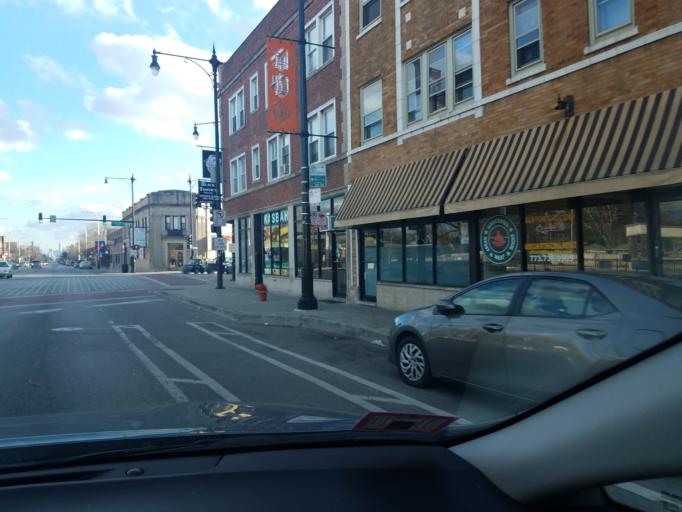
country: US
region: Illinois
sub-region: Cook County
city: Lincolnwood
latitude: 41.9598
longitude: -87.7281
